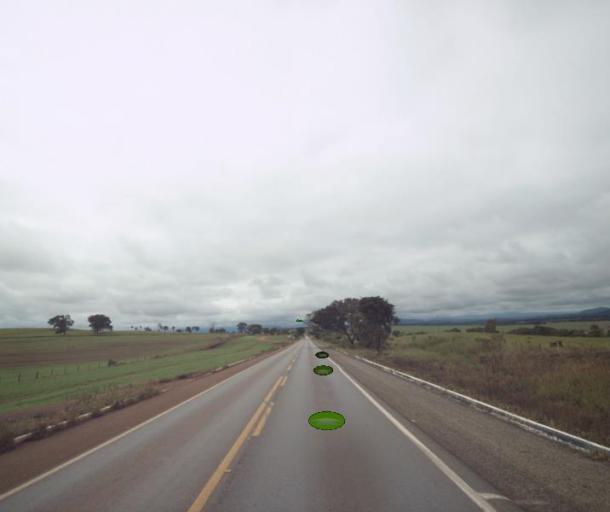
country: BR
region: Goias
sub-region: Uruacu
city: Uruacu
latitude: -14.6781
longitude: -49.1348
